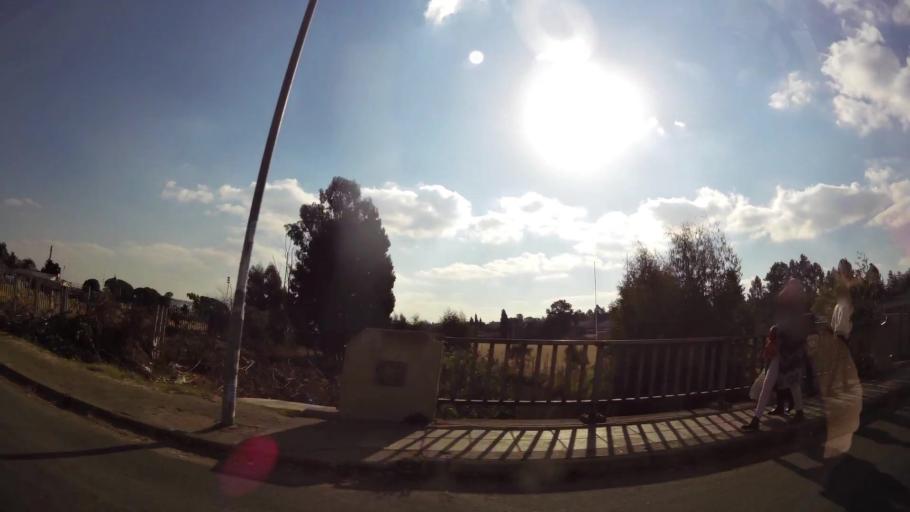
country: ZA
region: Gauteng
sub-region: West Rand District Municipality
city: Krugersdorp
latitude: -26.0965
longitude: 27.7754
